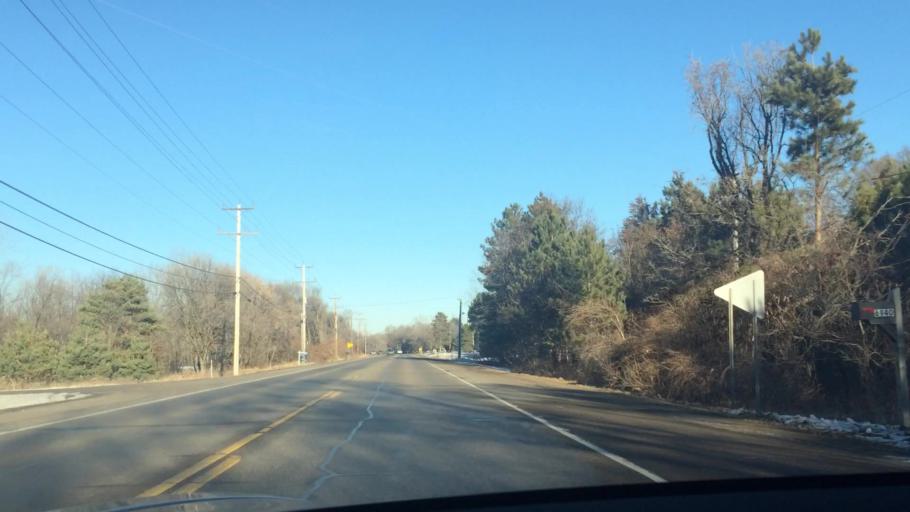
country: US
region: Minnesota
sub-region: Anoka County
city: Circle Pines
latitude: 45.1573
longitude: -93.1287
